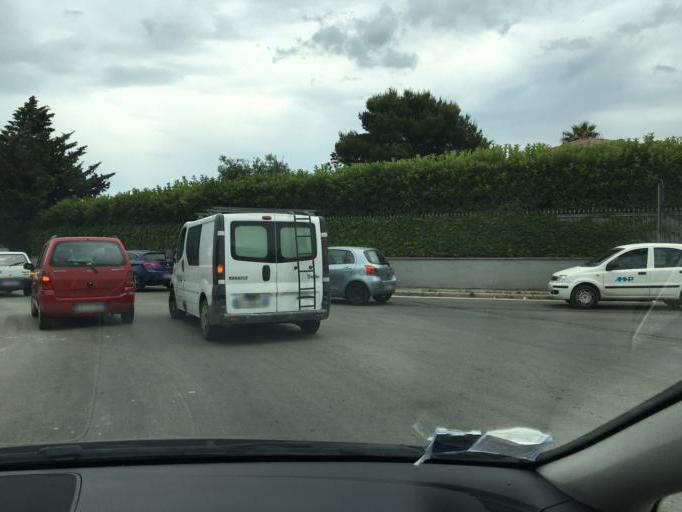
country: IT
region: Sicily
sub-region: Palermo
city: Isola delle Femmine
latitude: 38.1882
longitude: 13.3001
